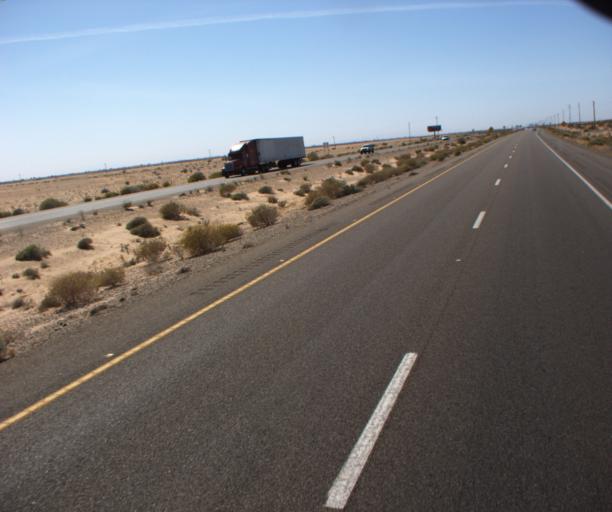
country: MX
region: Sonora
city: San Luis Rio Colorado
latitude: 32.4947
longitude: -114.6877
